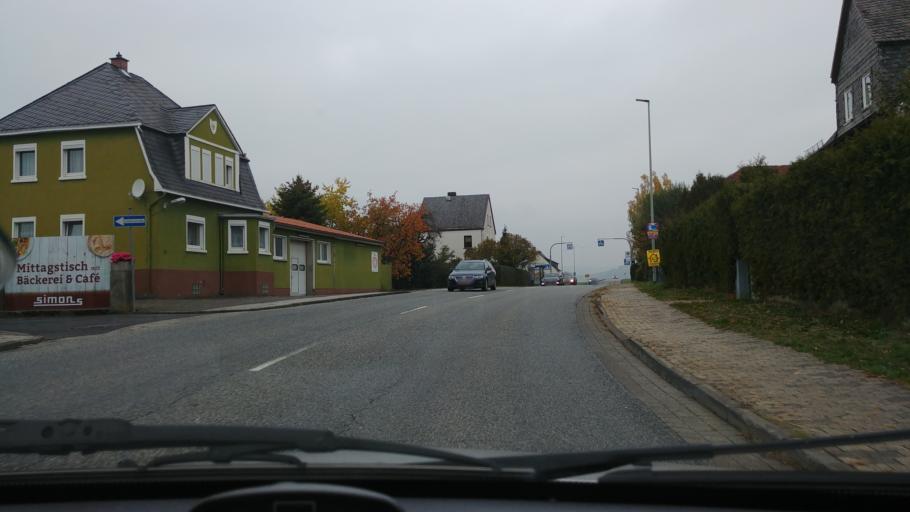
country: DE
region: Rheinland-Pfalz
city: Irmtraut
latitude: 50.5126
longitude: 8.0609
